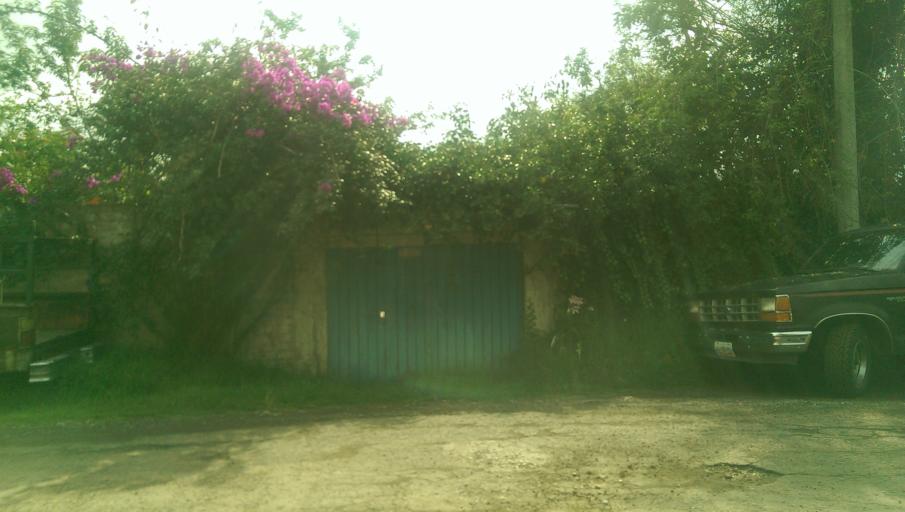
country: MX
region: Mexico
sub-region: Jilotepec
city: Jilotepec de Molina Enriquez
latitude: 19.9624
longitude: -99.4880
